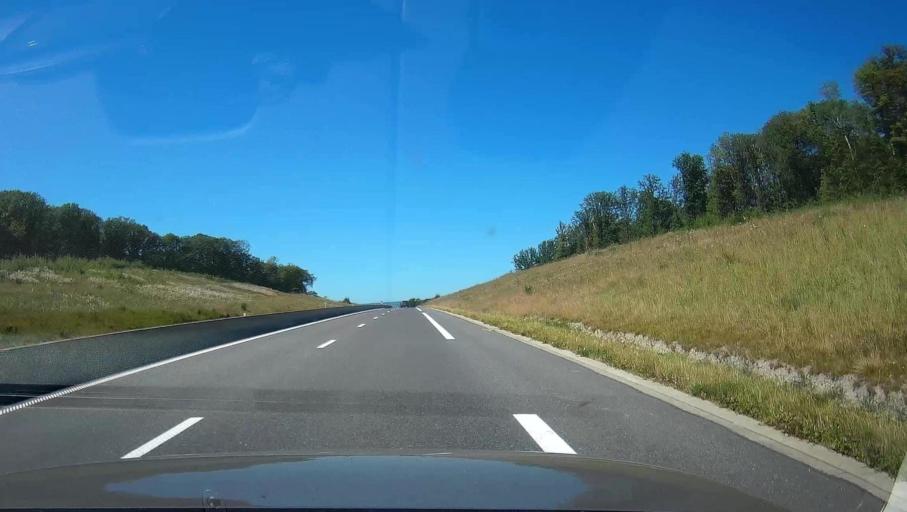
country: FR
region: Champagne-Ardenne
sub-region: Departement des Ardennes
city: Warcq
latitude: 49.7560
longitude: 4.6561
